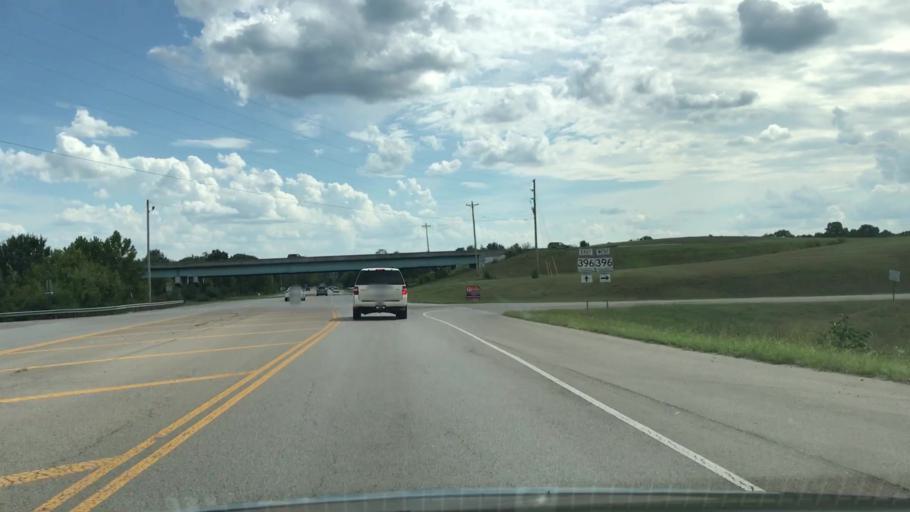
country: US
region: Tennessee
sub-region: Maury County
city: Spring Hill
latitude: 35.7344
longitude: -86.9248
